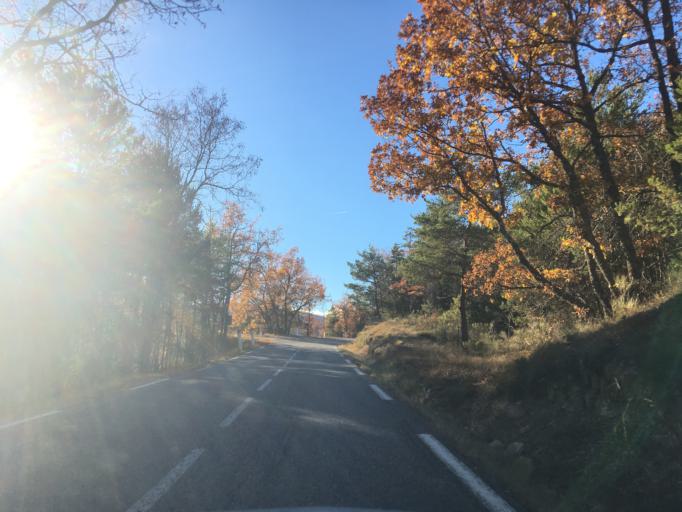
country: FR
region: Provence-Alpes-Cote d'Azur
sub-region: Departement des Alpes-de-Haute-Provence
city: Castellane
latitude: 43.7413
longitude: 6.4931
